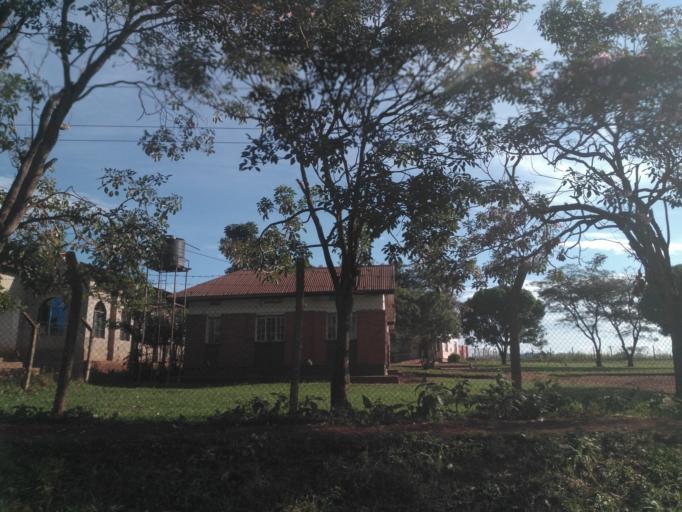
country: UG
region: Eastern Region
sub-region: Jinja District
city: Jinja
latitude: 0.4525
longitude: 33.1905
